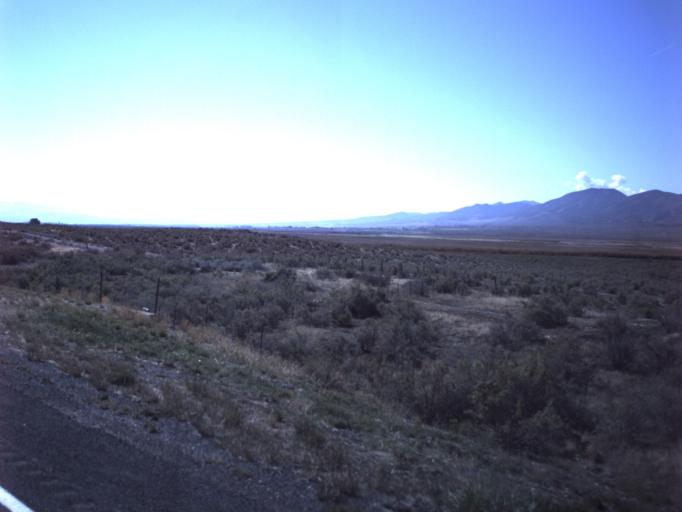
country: US
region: Utah
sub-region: Sanpete County
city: Gunnison
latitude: 39.2927
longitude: -111.8881
